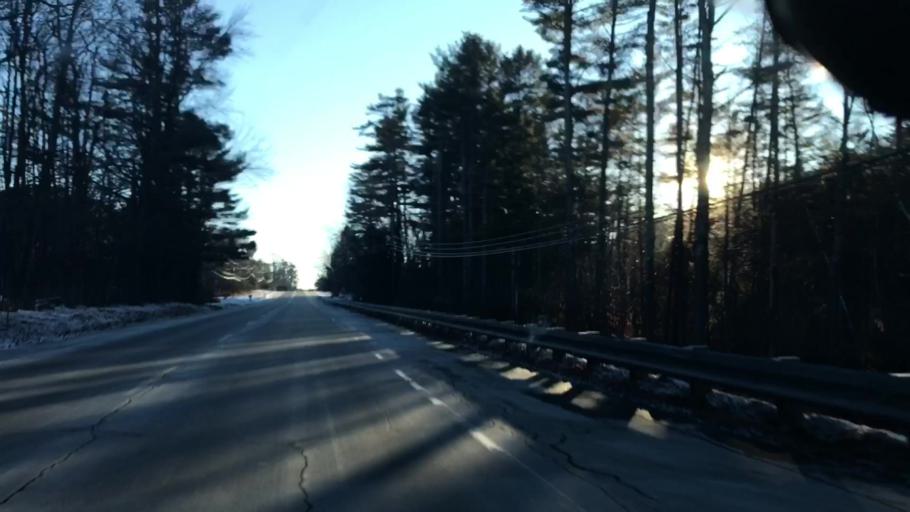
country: US
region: New Hampshire
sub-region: Grafton County
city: Lyme
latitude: 43.7993
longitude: -72.1681
